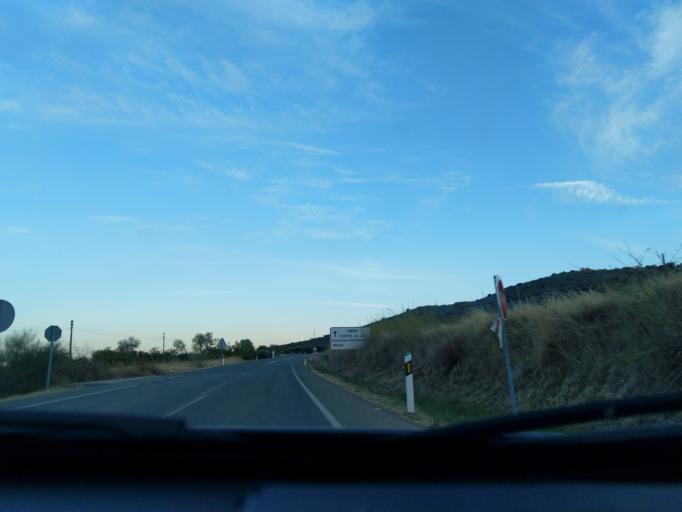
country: ES
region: Extremadura
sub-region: Provincia de Badajoz
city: Reina
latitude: 38.1905
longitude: -5.9465
